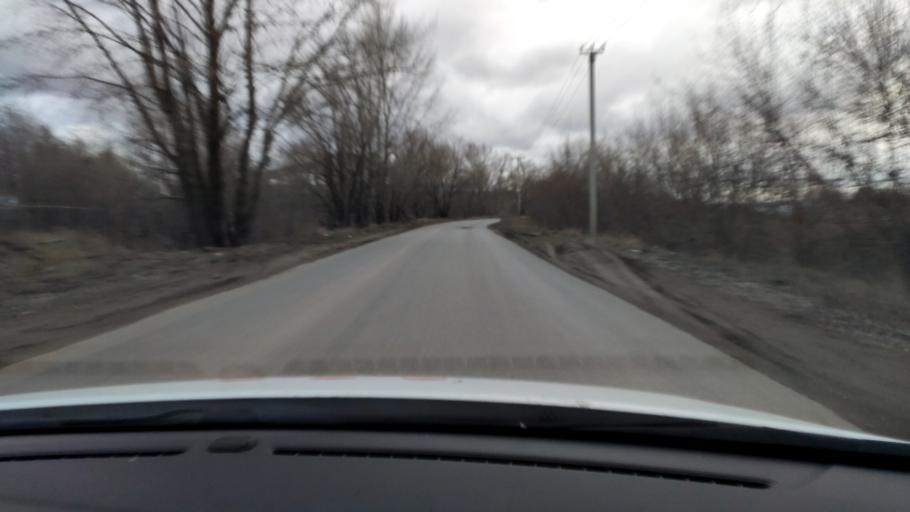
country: RU
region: Tatarstan
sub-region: Gorod Kazan'
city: Kazan
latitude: 55.7237
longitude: 49.0951
